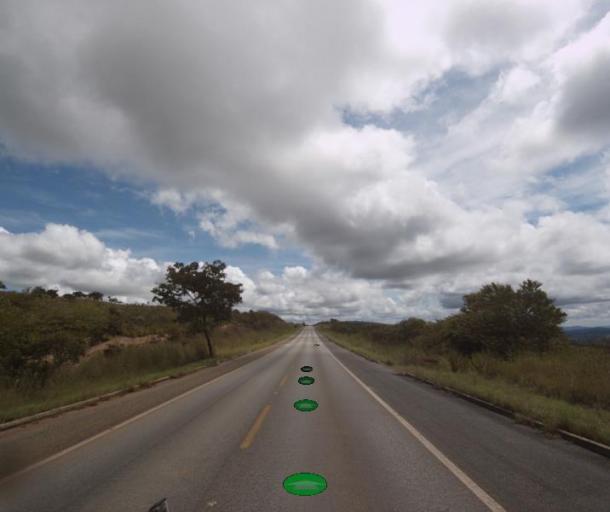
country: BR
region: Goias
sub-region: Abadiania
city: Abadiania
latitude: -15.7817
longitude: -48.4906
